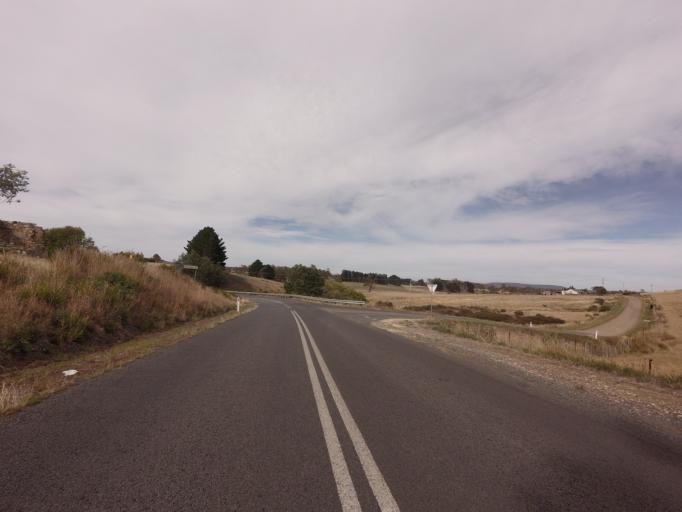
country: AU
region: Tasmania
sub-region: Sorell
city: Sorell
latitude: -42.4293
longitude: 147.4658
